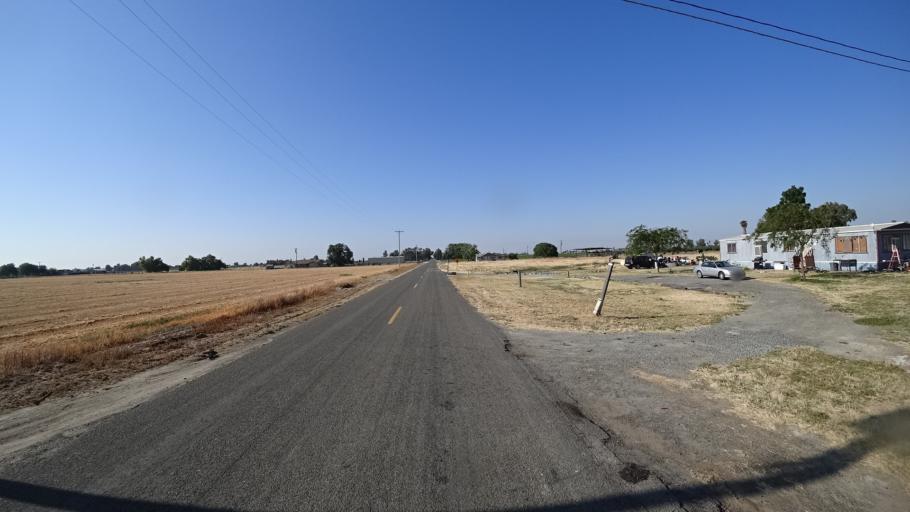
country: US
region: California
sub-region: Fresno County
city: Riverdale
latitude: 36.3604
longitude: -119.8693
